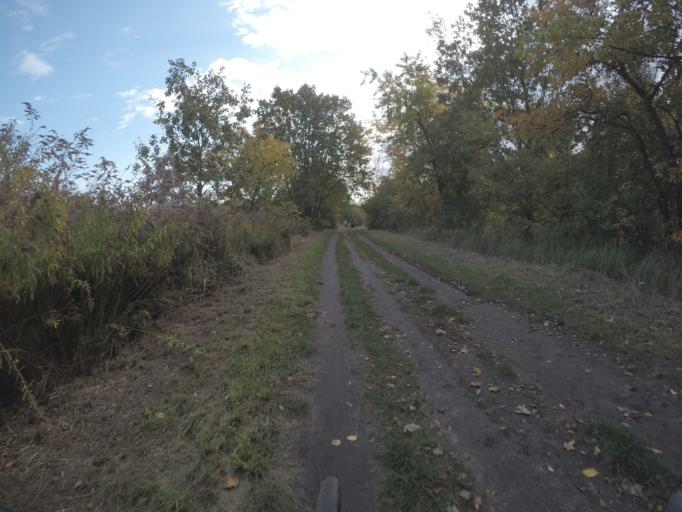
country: DE
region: Berlin
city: Frohnau
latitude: 52.6427
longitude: 13.2615
